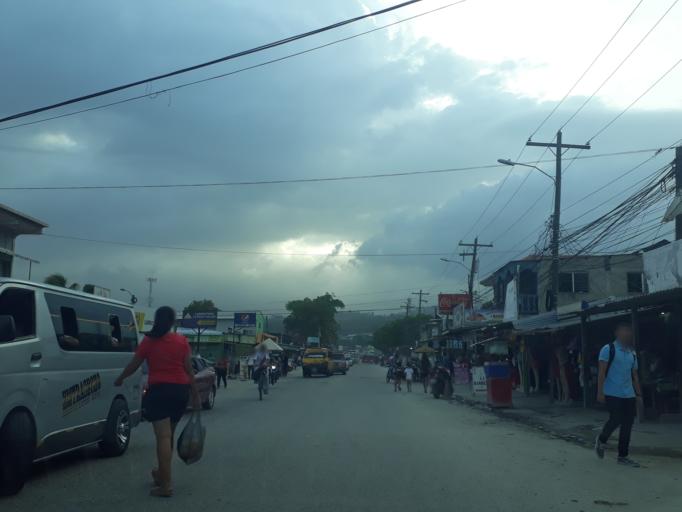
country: HN
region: Cortes
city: Choloma
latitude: 15.5727
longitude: -87.9507
